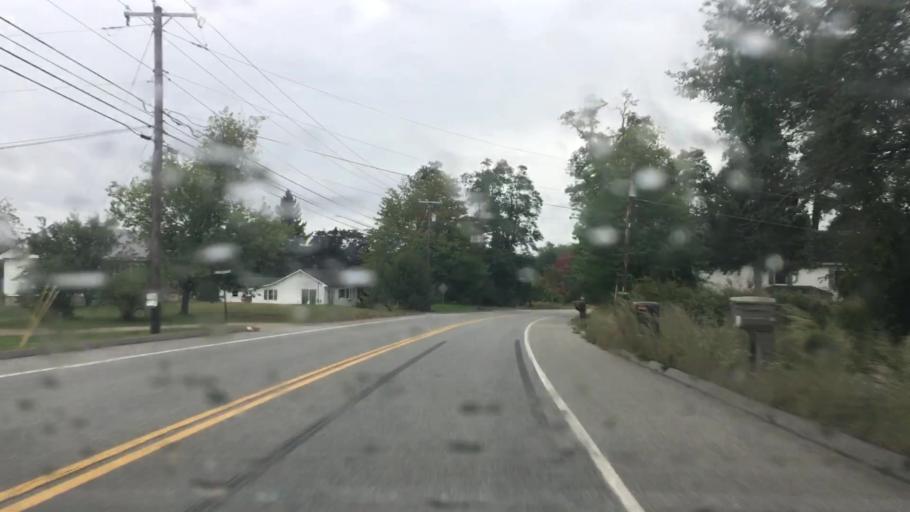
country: US
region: Maine
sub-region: Penobscot County
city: Orrington
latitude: 44.7225
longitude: -68.8262
